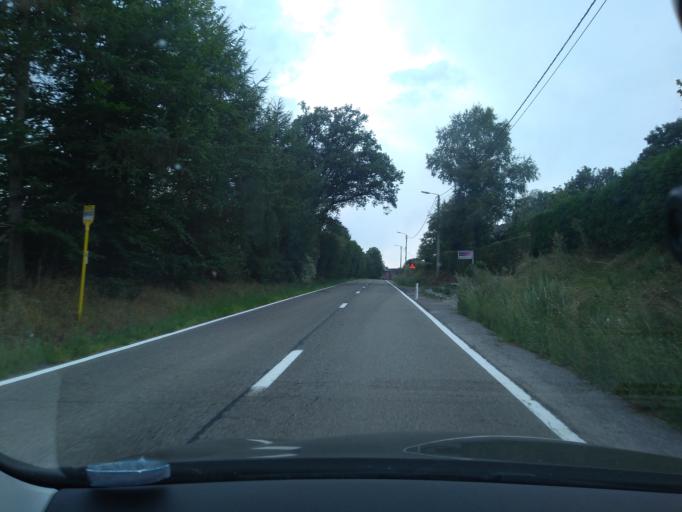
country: BE
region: Wallonia
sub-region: Province du Luxembourg
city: Bertogne
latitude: 50.0711
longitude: 5.6415
